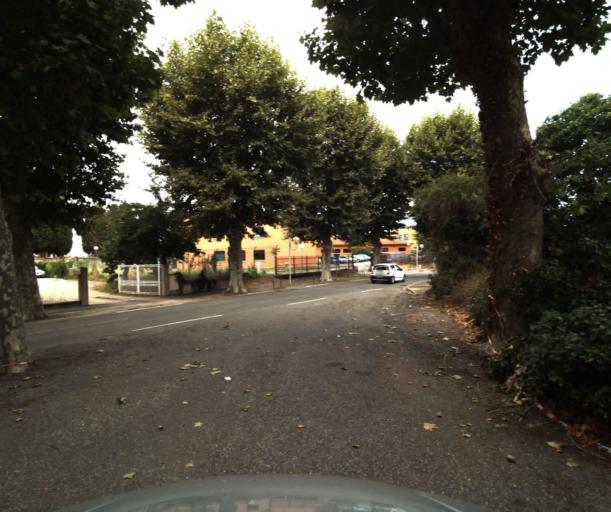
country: FR
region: Midi-Pyrenees
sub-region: Departement de la Haute-Garonne
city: Muret
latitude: 43.4667
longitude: 1.3249
